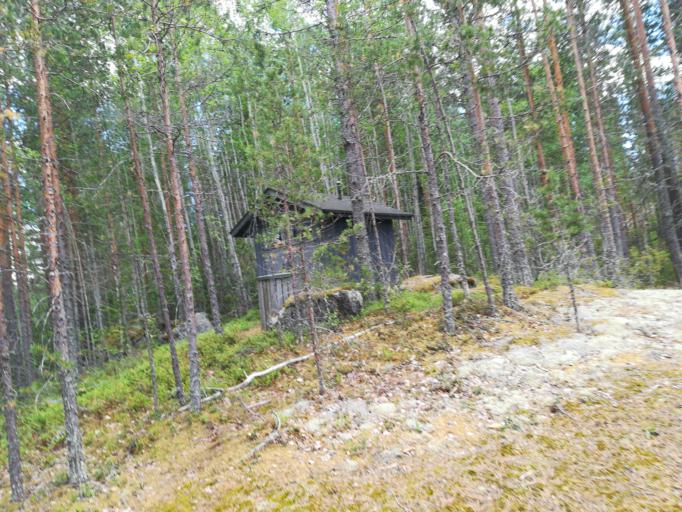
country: FI
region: Southern Savonia
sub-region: Mikkeli
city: Hirvensalmi
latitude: 61.7088
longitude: 26.9714
